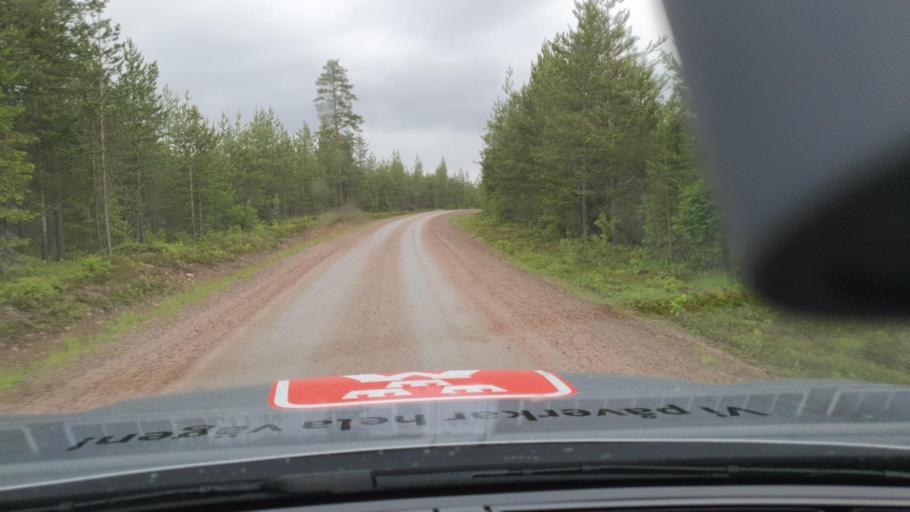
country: SE
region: Norrbotten
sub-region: Overkalix Kommun
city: OEverkalix
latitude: 66.6410
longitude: 22.7012
